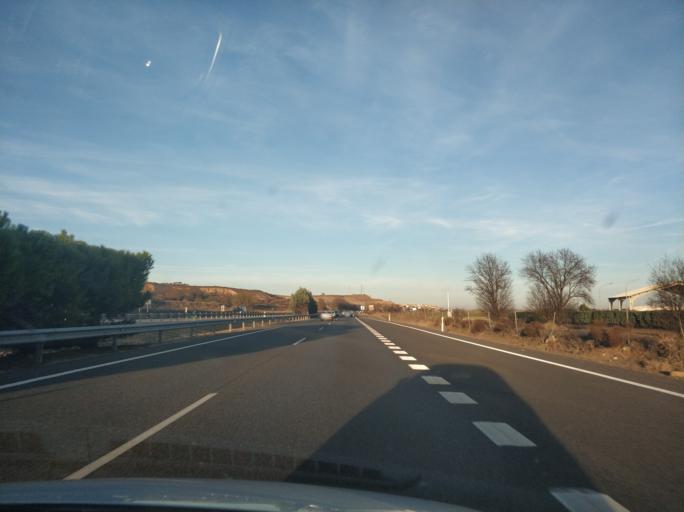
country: ES
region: Castille and Leon
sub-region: Provincia de Valladolid
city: Simancas
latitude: 41.5746
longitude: -4.8487
